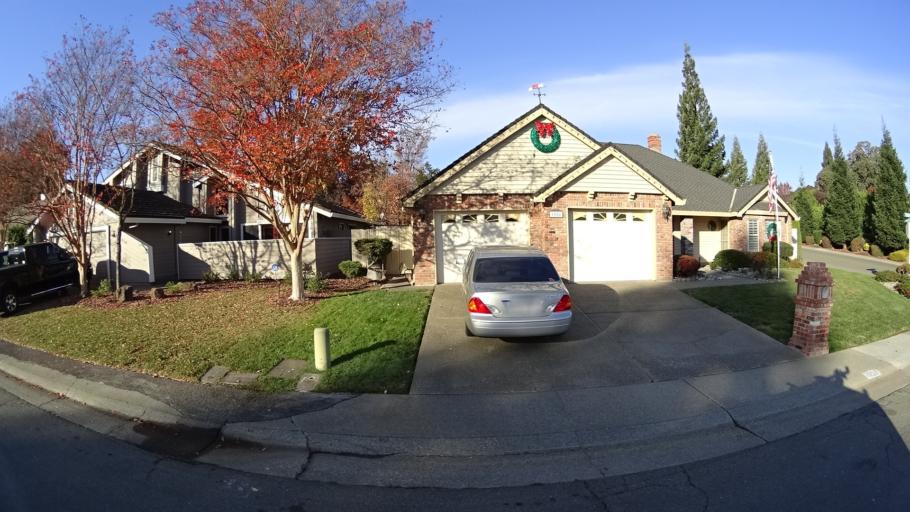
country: US
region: California
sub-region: Sacramento County
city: Citrus Heights
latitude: 38.7238
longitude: -121.2761
